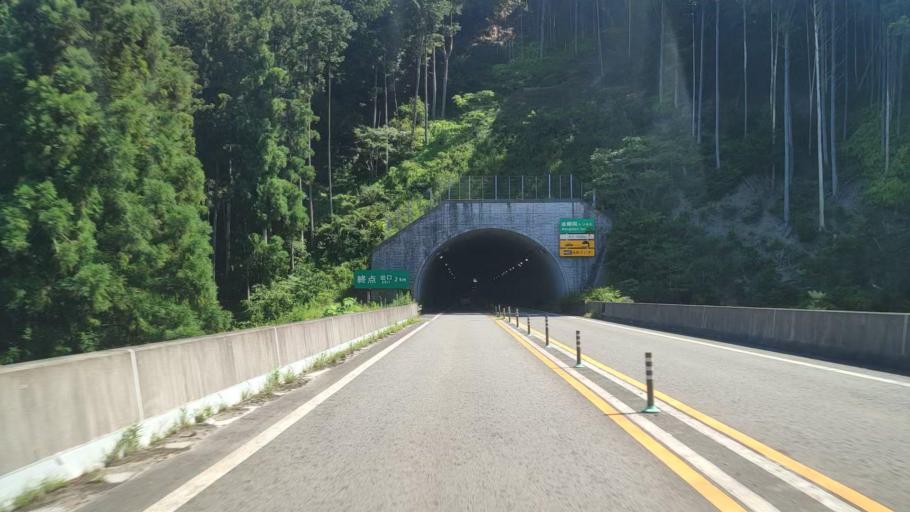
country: JP
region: Wakayama
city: Shingu
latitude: 33.6086
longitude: 135.9166
